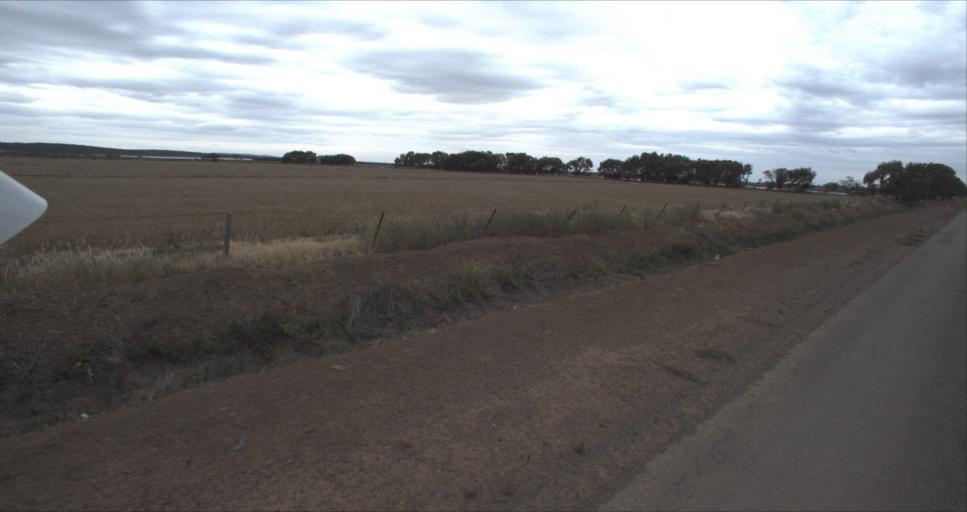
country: AU
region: New South Wales
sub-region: Leeton
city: Leeton
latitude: -34.4107
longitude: 146.3404
